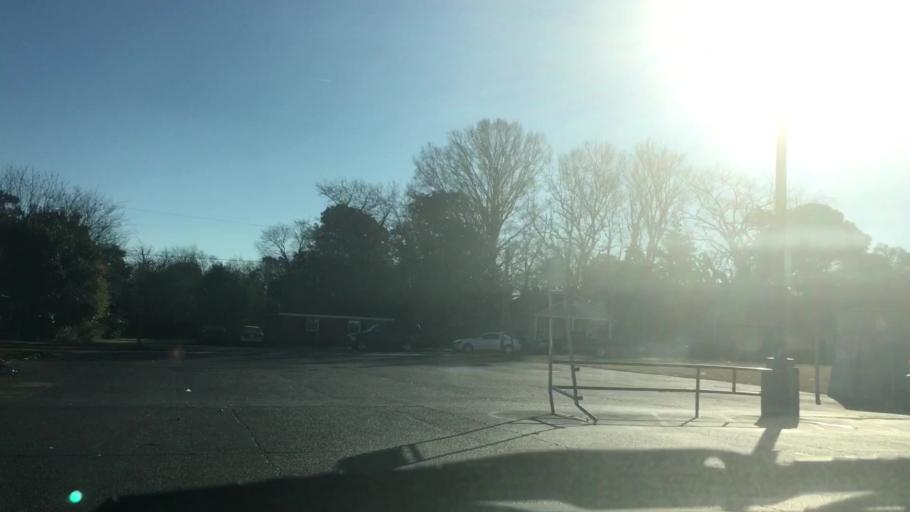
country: US
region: Virginia
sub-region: City of Norfolk
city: Norfolk
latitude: 36.8789
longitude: -76.2628
